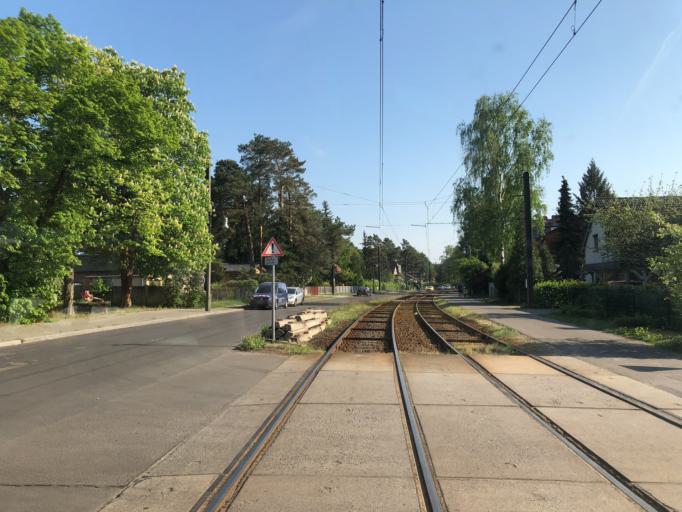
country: DE
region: Berlin
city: Schmockwitz
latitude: 52.3909
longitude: 13.6350
